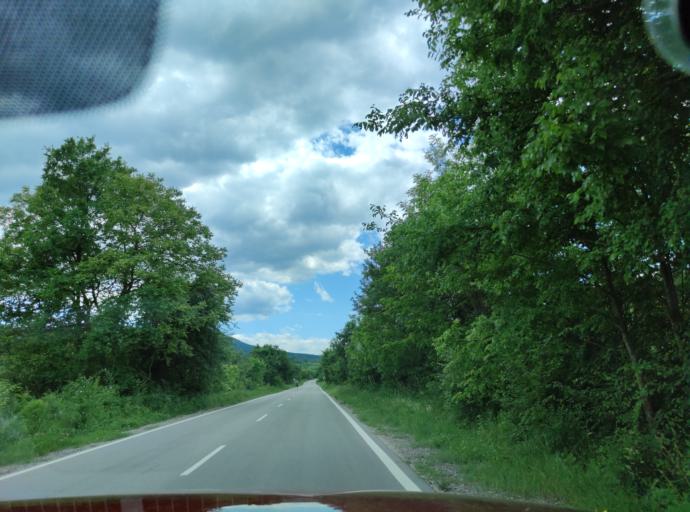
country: BG
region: Montana
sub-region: Obshtina Chiprovtsi
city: Chiprovtsi
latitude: 43.4484
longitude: 22.9153
